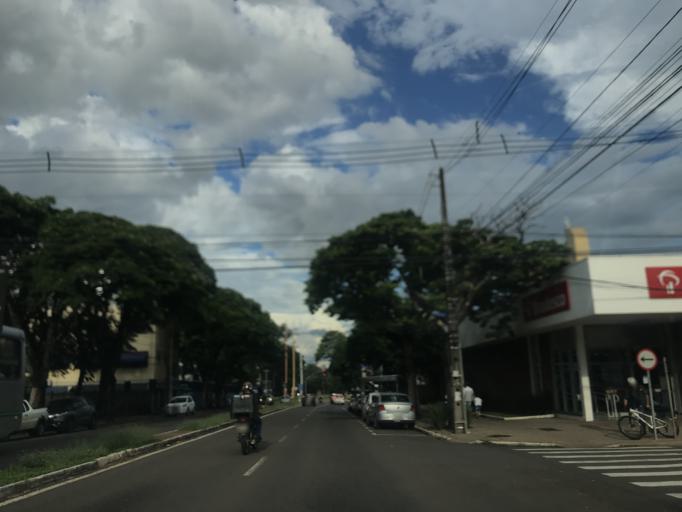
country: BR
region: Parana
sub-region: Maringa
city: Maringa
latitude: -23.4231
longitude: -51.9551
